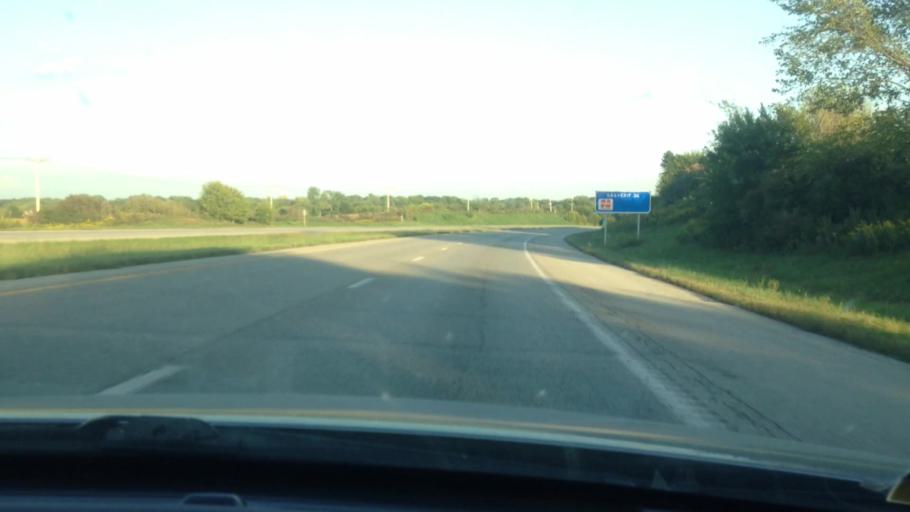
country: US
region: Missouri
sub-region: Platte County
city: Weatherby Lake
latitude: 39.3156
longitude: -94.6802
